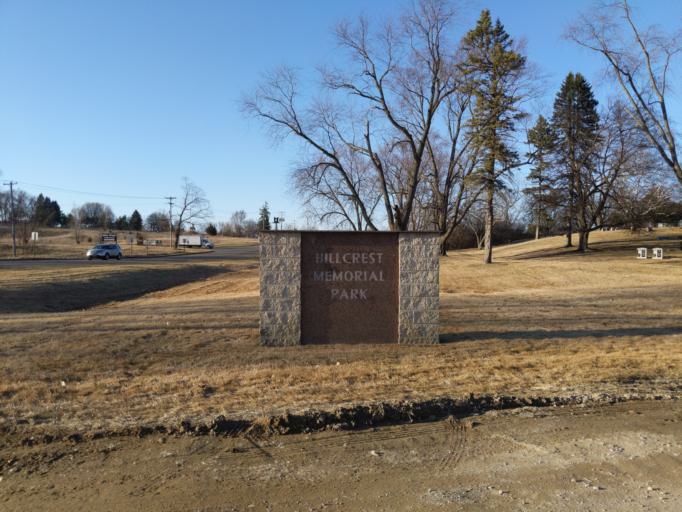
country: US
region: Michigan
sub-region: Jackson County
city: Jackson
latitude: 42.2713
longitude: -84.3841
